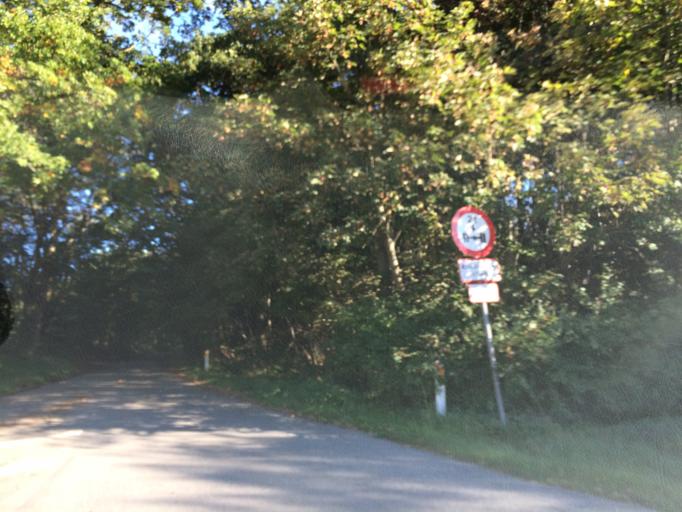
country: DK
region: Central Jutland
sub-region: Randers Kommune
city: Langa
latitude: 56.3535
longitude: 9.9268
